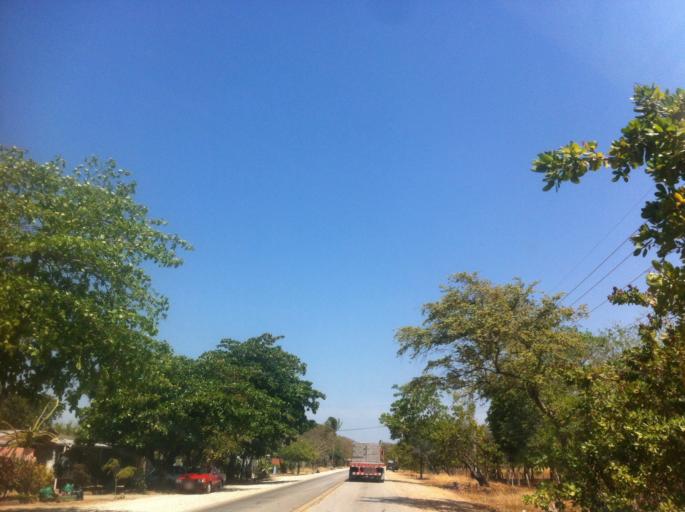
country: CR
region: Guanacaste
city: Santa Cruz
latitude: 10.2560
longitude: -85.5644
